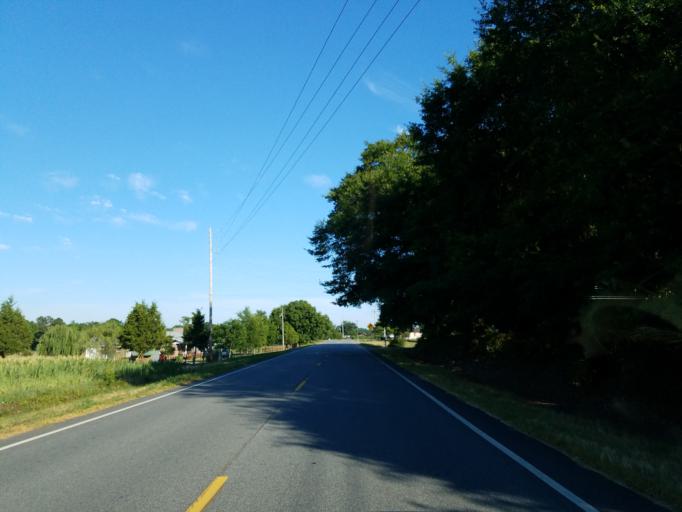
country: US
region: Georgia
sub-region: Gordon County
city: Calhoun
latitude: 34.5809
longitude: -85.0285
